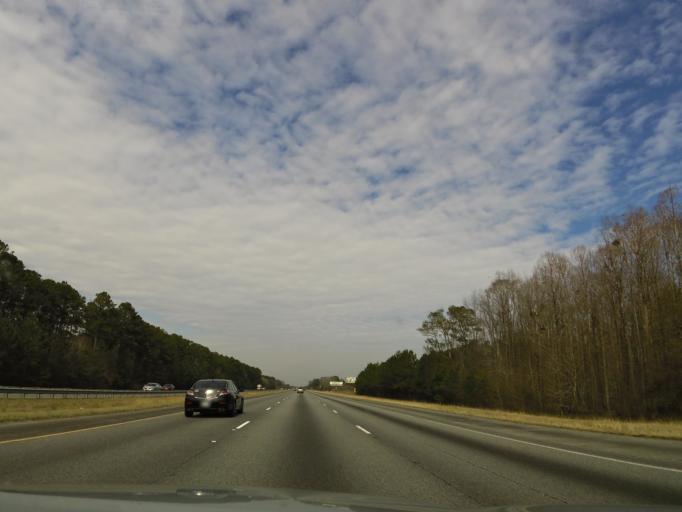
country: US
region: Georgia
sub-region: Liberty County
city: Midway
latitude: 31.5901
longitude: -81.4264
